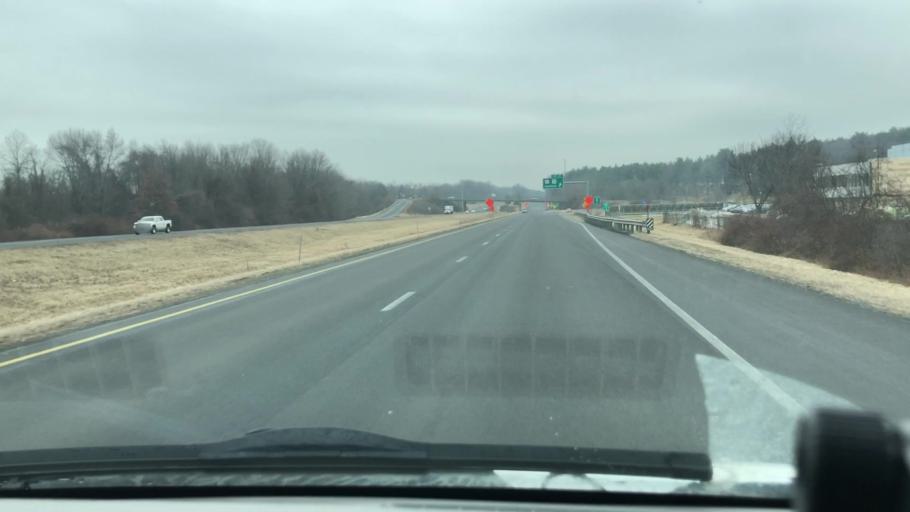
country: US
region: Massachusetts
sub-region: Hampshire County
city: Hatfield
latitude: 42.3657
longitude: -72.6353
